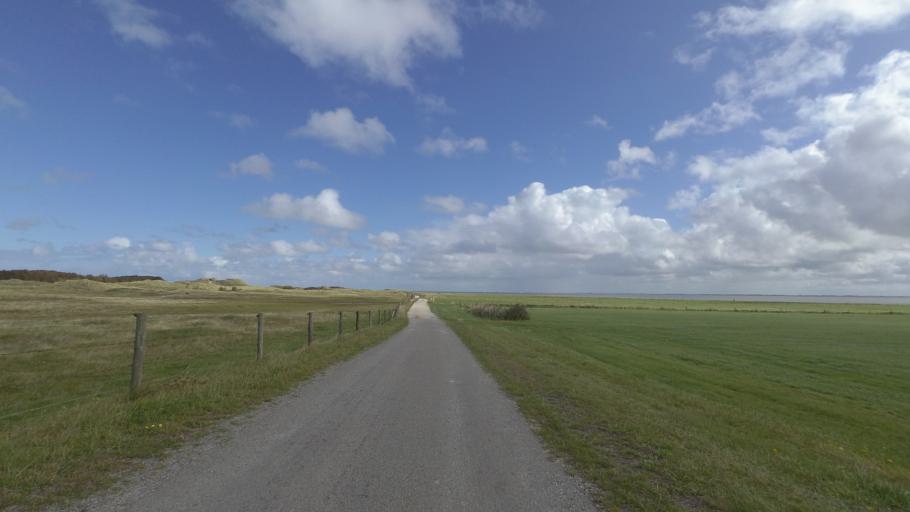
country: NL
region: Friesland
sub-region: Gemeente Ameland
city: Nes
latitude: 53.4474
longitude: 5.8506
